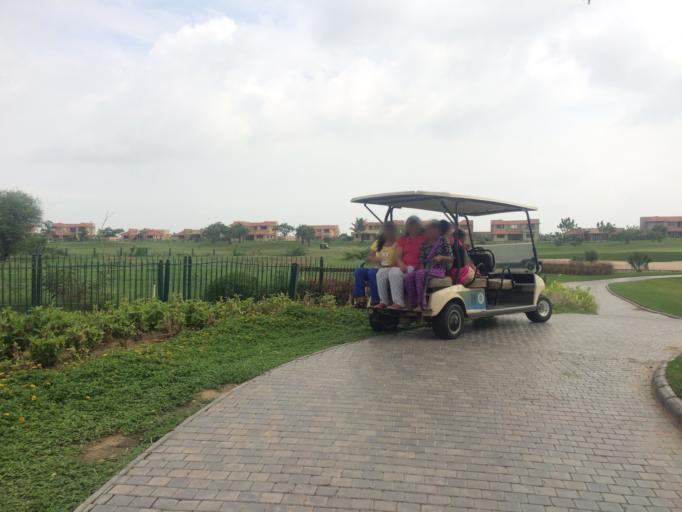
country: IN
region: Gujarat
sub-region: Ahmadabad
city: Sanand
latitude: 23.0215
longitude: 72.3554
